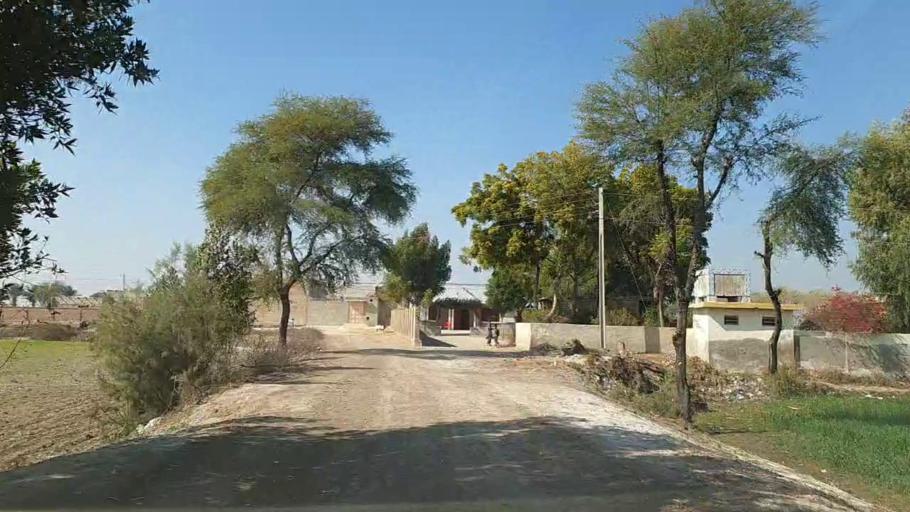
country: PK
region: Sindh
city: Nawabshah
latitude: 26.2825
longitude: 68.3719
